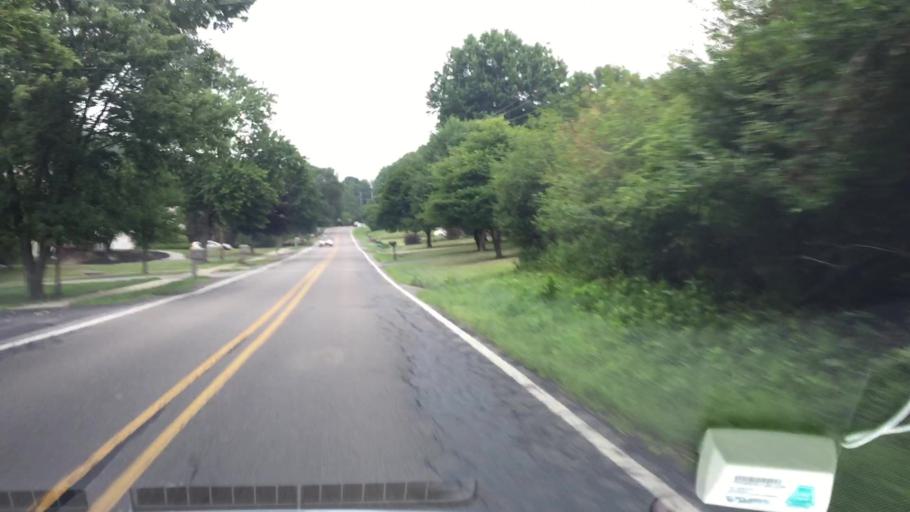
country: US
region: Pennsylvania
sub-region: Allegheny County
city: Franklin Park
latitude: 40.6058
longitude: -80.0754
